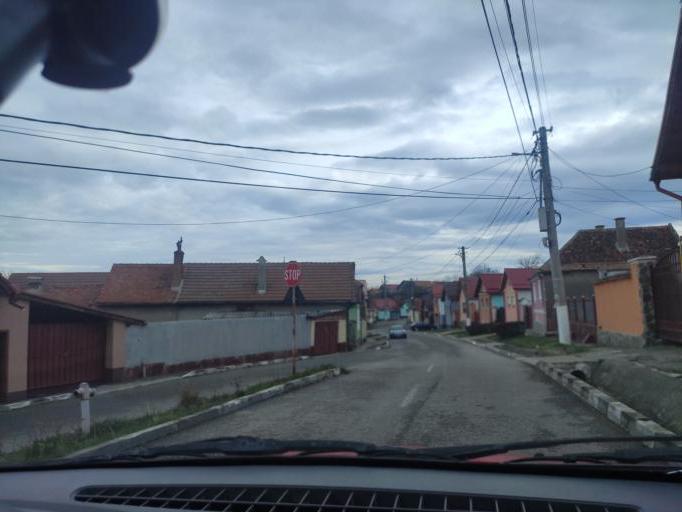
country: RO
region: Brasov
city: Codlea
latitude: 45.6954
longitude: 25.4364
